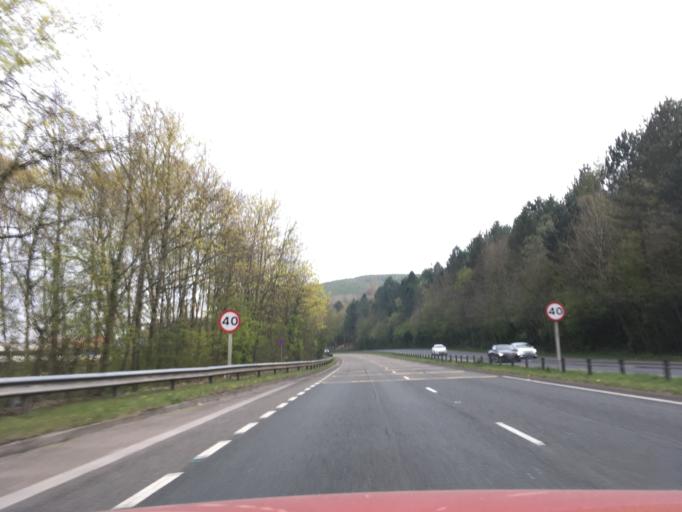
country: GB
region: Wales
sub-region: Caerphilly County Borough
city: Risca
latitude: 51.6030
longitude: -3.0993
